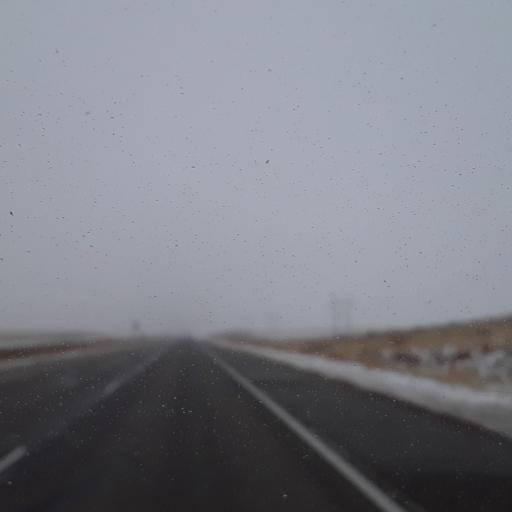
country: US
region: Nebraska
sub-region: Cheyenne County
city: Sidney
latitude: 40.7971
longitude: -102.8752
